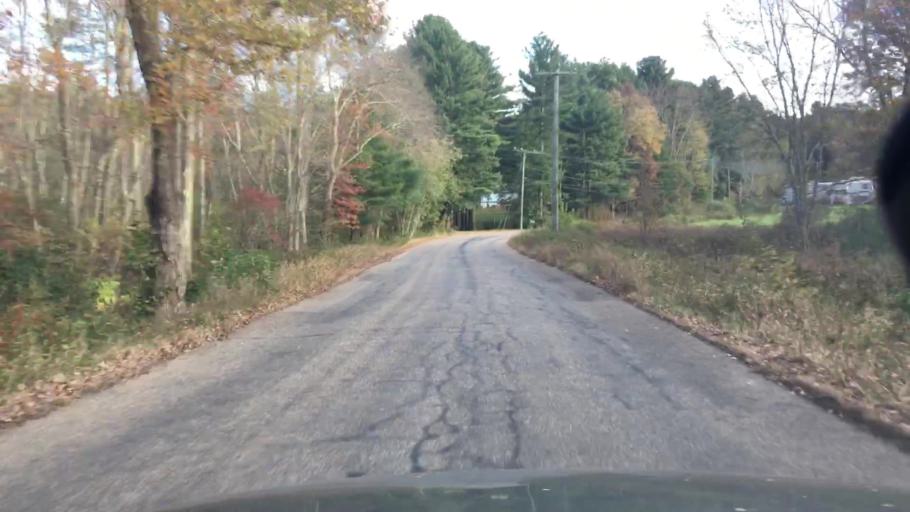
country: US
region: Connecticut
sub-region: Tolland County
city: Stafford
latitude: 41.9702
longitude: -72.2891
